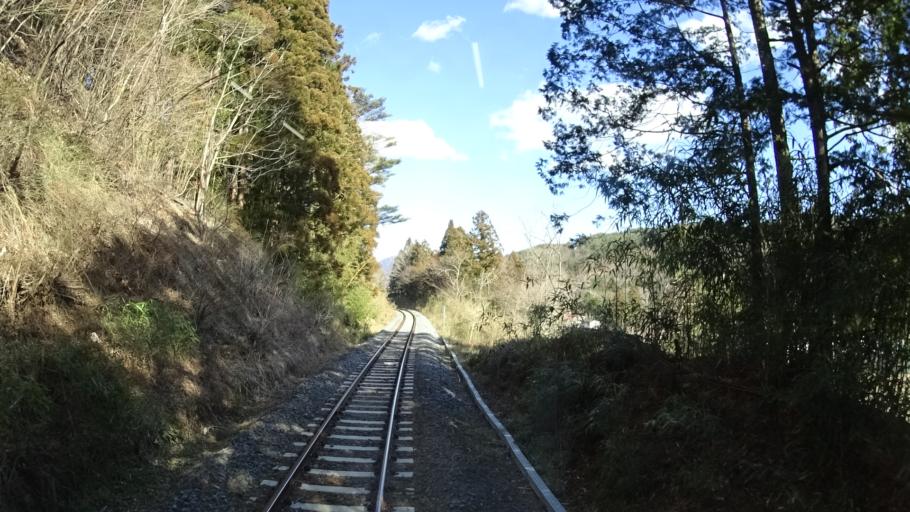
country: JP
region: Iwate
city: Yamada
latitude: 39.4763
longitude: 141.9356
